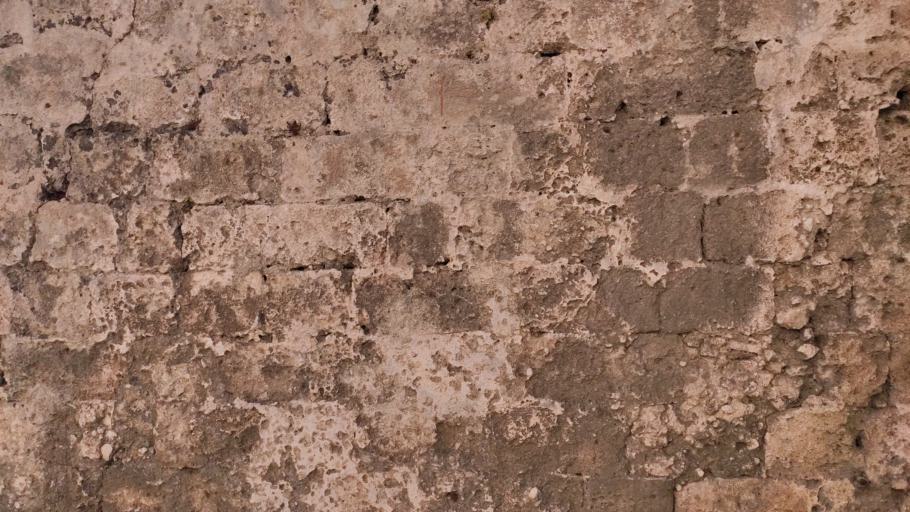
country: GR
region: South Aegean
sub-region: Nomos Dodekanisou
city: Rodos
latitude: 36.4402
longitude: 28.2285
